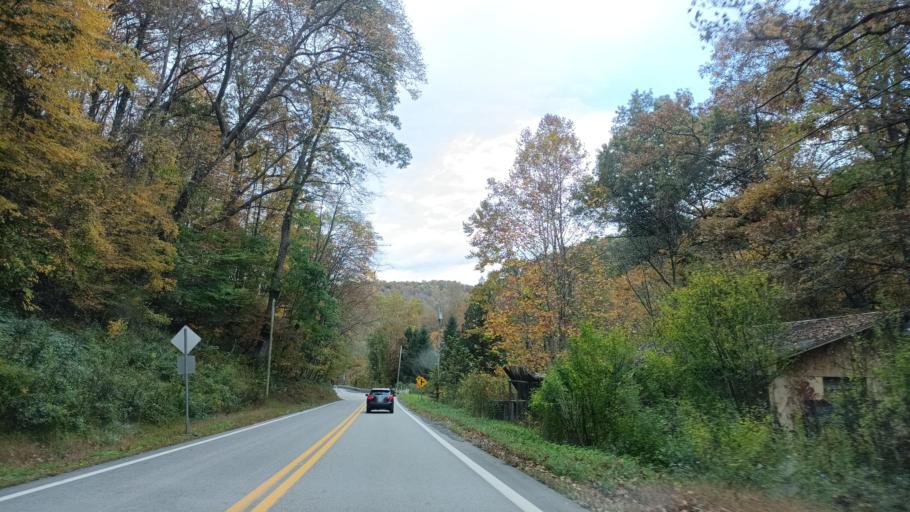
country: US
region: West Virginia
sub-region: Taylor County
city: Grafton
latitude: 39.3435
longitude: -79.9379
